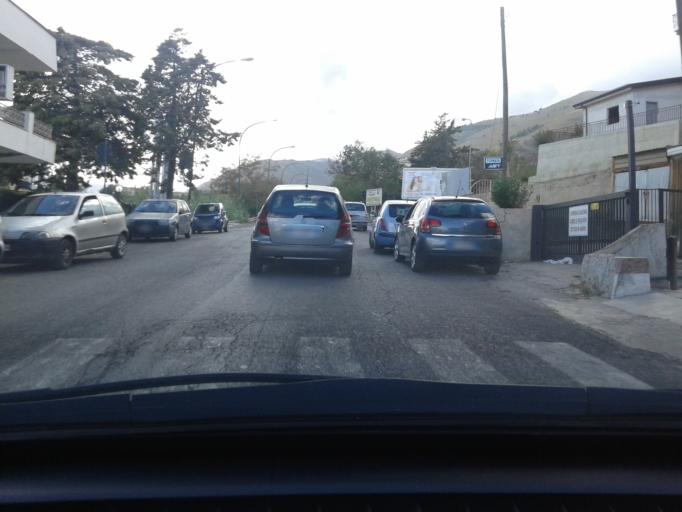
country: IT
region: Sicily
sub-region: Palermo
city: Monreale
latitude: 38.0774
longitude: 13.2922
